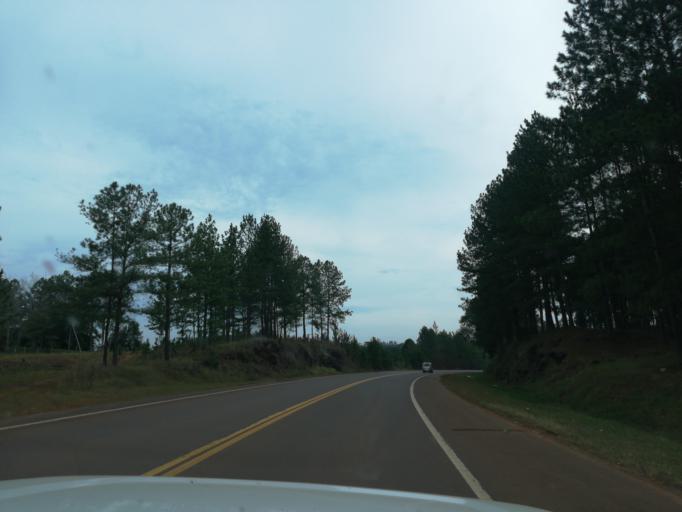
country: AR
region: Misiones
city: San Vicente
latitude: -26.6356
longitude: -54.1272
